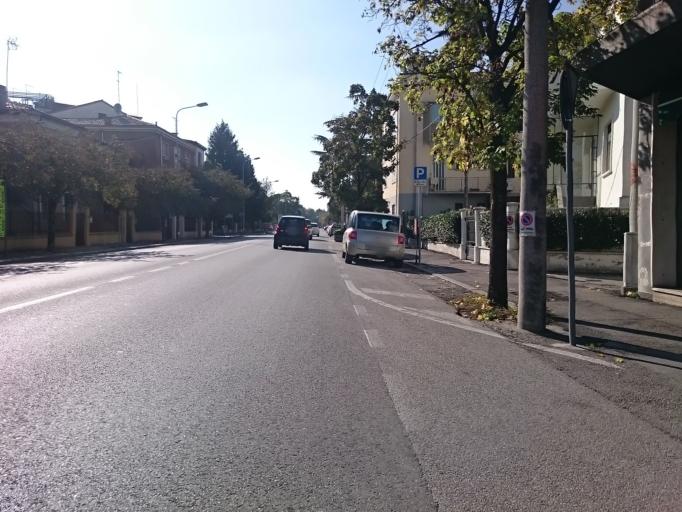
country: IT
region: Veneto
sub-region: Provincia di Padova
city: Padova
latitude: 45.4028
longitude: 11.8607
